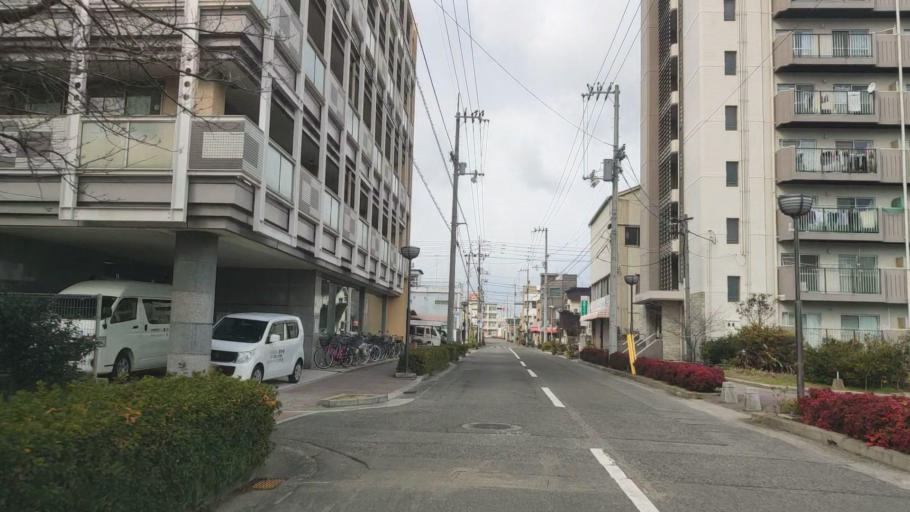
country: JP
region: Ehime
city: Saijo
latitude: 34.0629
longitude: 133.0052
